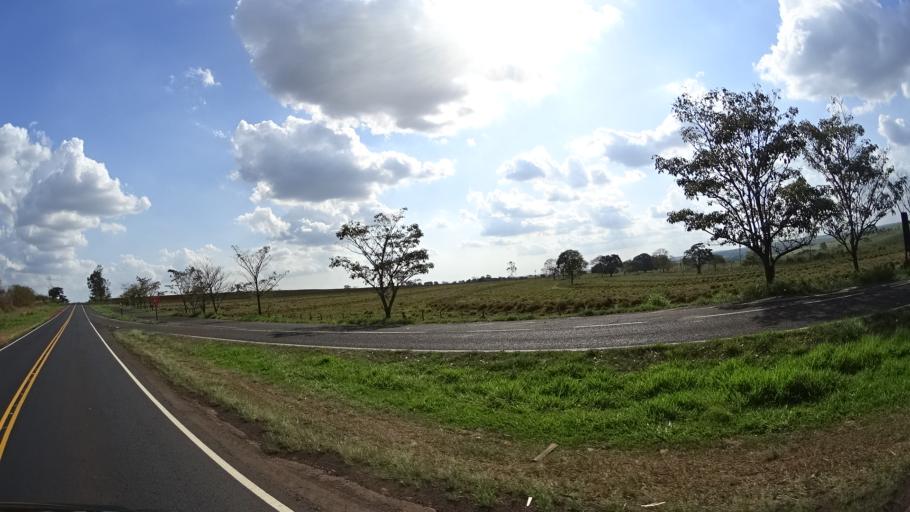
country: BR
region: Sao Paulo
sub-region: Urupes
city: Urupes
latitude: -21.1035
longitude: -49.2637
